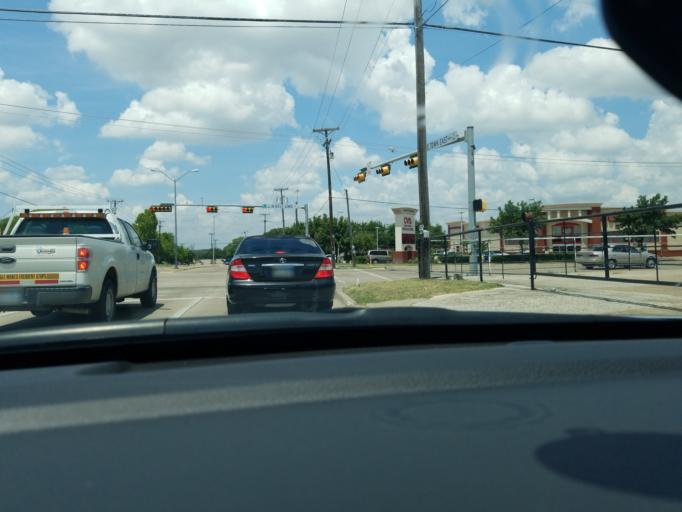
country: US
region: Texas
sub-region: Dallas County
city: Sunnyvale
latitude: 32.8140
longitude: -96.5956
